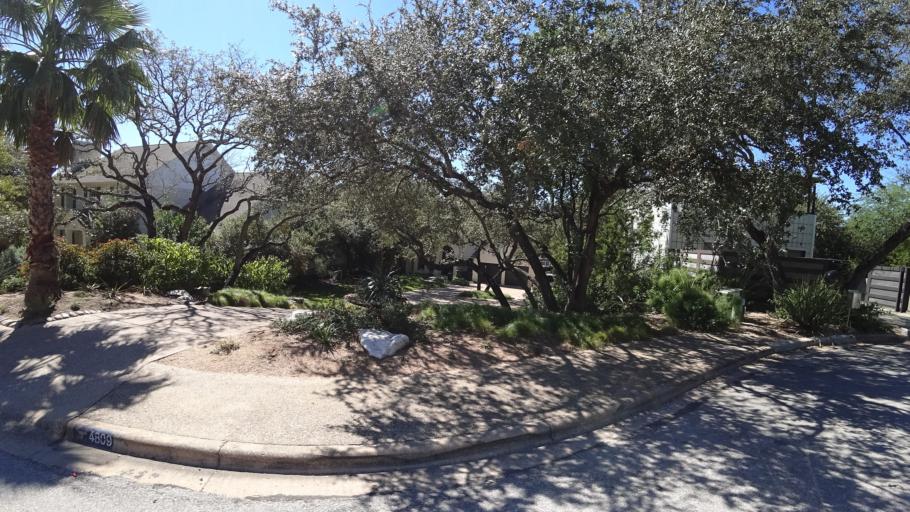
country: US
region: Texas
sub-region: Travis County
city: West Lake Hills
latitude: 30.3426
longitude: -97.7846
